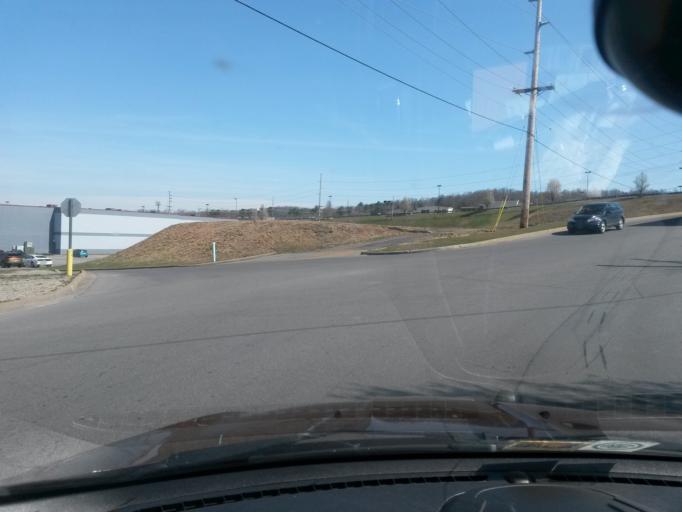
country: US
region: West Virginia
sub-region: Raleigh County
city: Beckley
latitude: 37.8017
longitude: -81.1775
